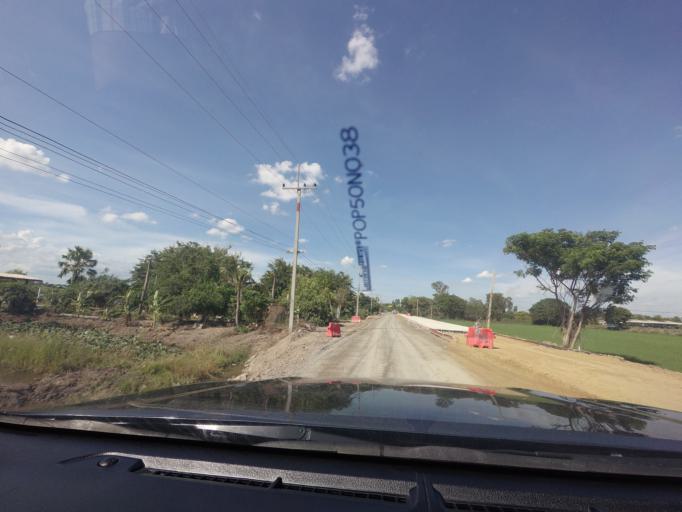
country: TH
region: Suphan Buri
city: Song Phi Nong
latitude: 14.1806
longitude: 100.0447
